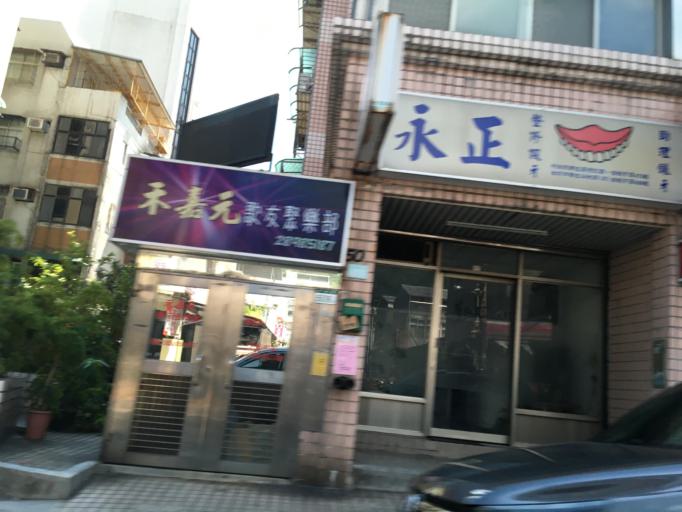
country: TW
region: Taipei
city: Taipei
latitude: 25.1453
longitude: 121.4942
